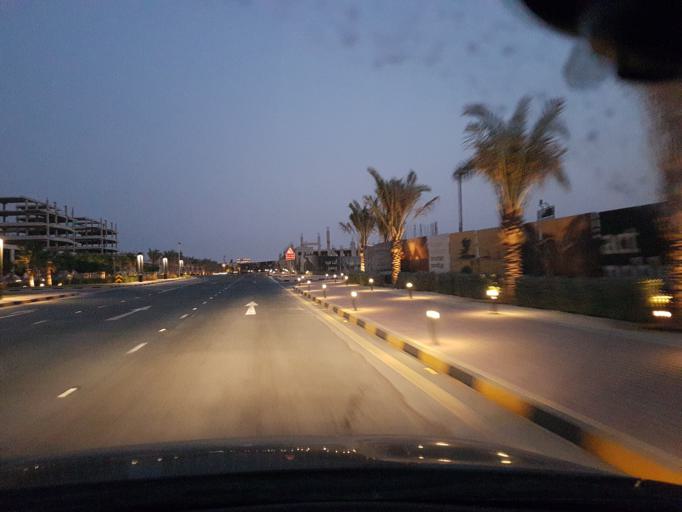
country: BH
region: Central Governorate
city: Dar Kulayb
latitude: 26.0147
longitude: 50.5121
